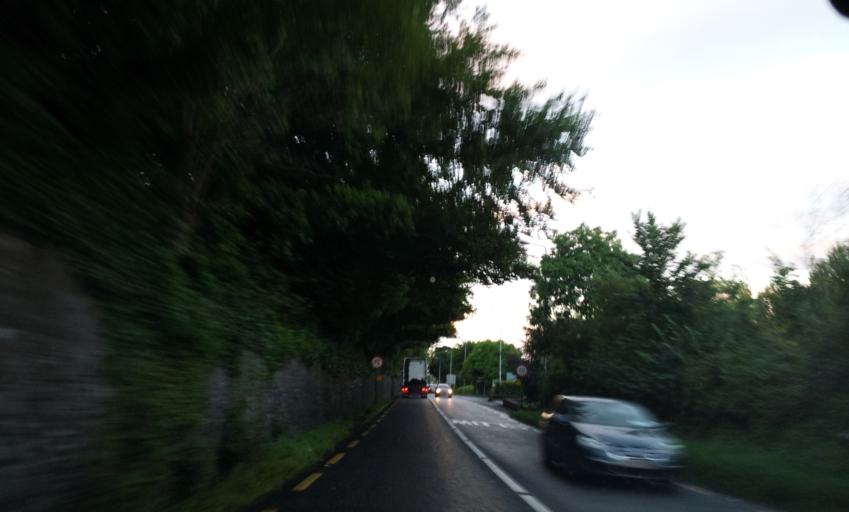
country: IE
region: Munster
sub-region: County Limerick
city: Adare
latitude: 52.5540
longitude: -8.8055
